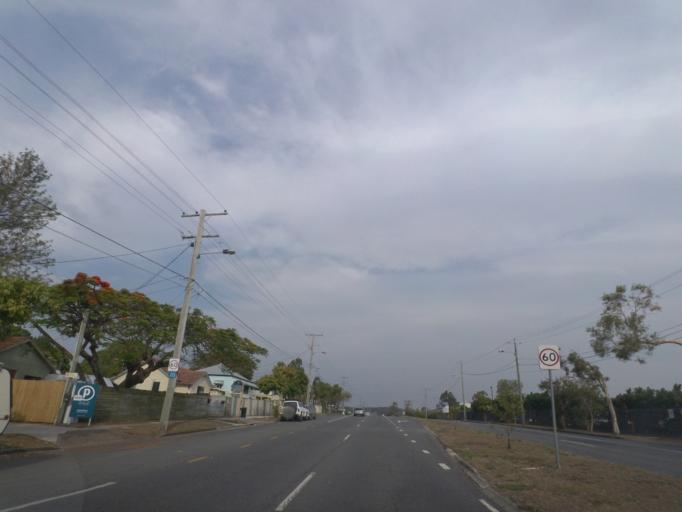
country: AU
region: Queensland
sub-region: Brisbane
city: Tarragindi
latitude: -27.5437
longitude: 153.0226
